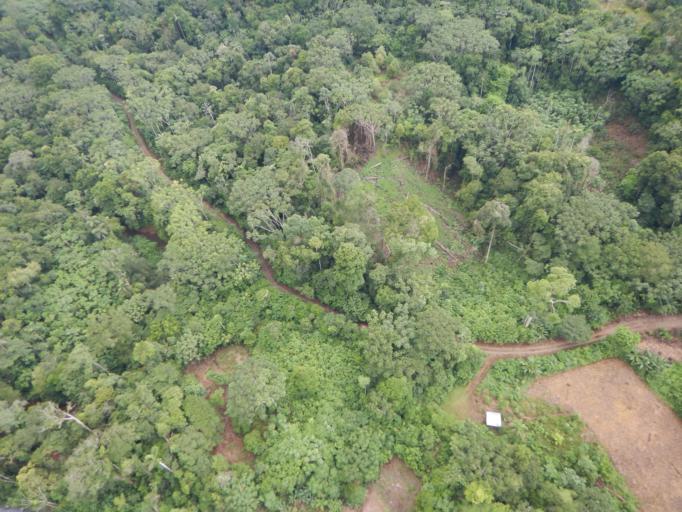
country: BO
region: Santa Cruz
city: Comarapa
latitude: -17.3126
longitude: -64.5846
